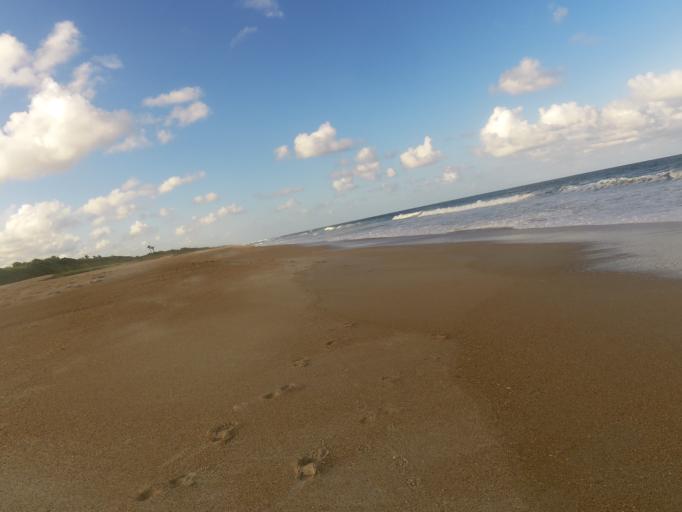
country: US
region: Florida
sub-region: Saint Johns County
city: Palm Valley
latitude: 30.0943
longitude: -81.3391
